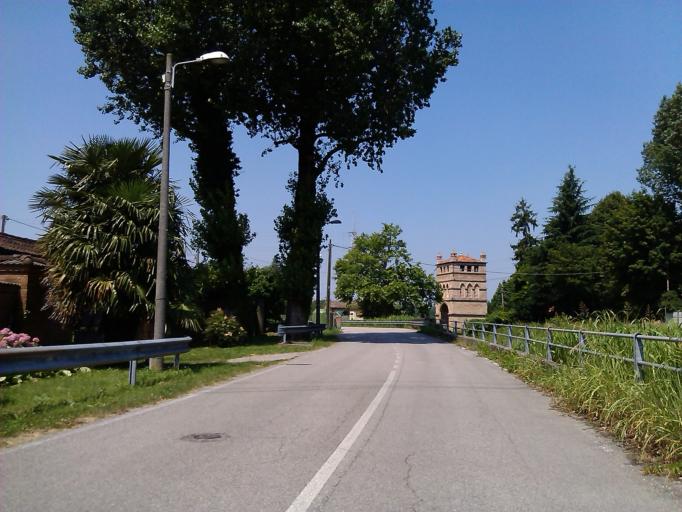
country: IT
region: Veneto
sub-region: Provincia di Venezia
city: Mestre
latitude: 45.4572
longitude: 12.2042
